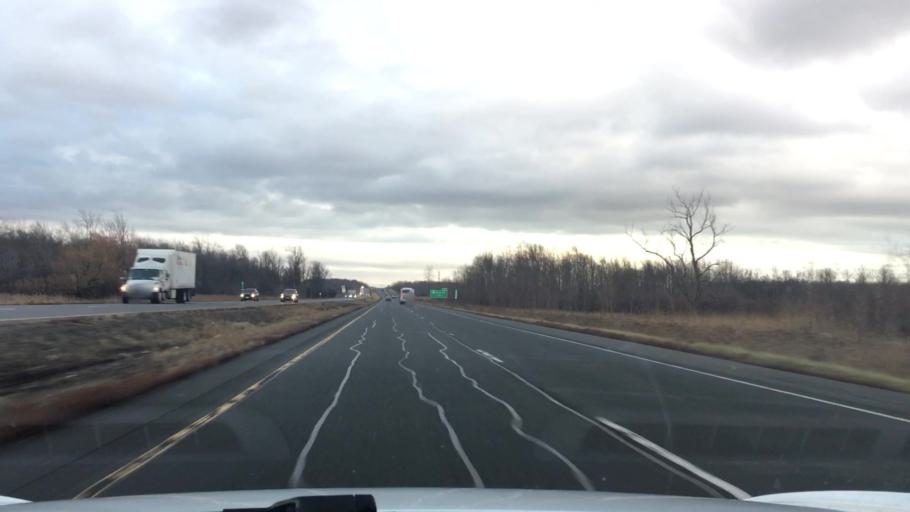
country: US
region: New York
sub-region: Erie County
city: Grandyle Village
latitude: 42.9452
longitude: -78.9982
